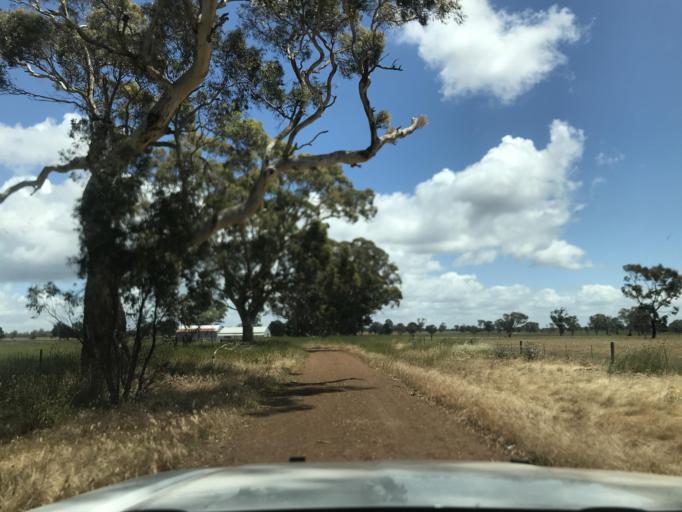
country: AU
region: South Australia
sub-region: Wattle Range
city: Penola
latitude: -37.0747
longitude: 141.3352
